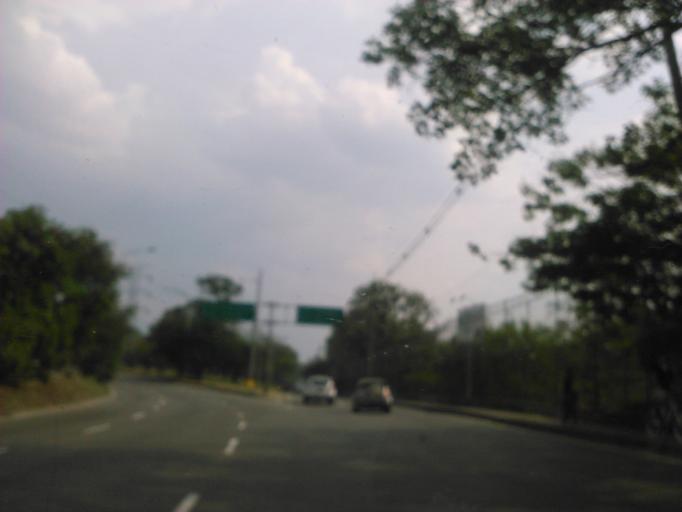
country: CO
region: Antioquia
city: Medellin
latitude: 6.2635
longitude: -75.5751
